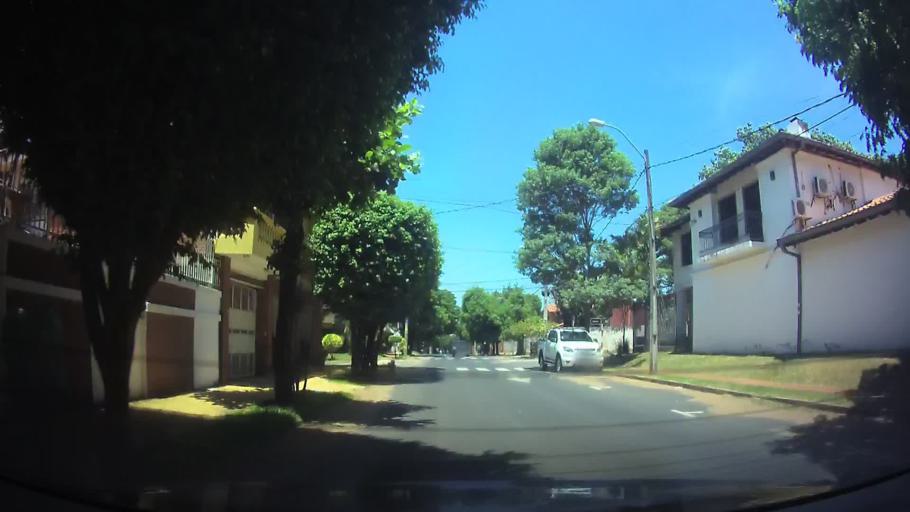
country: PY
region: Asuncion
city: Asuncion
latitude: -25.3021
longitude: -57.6027
